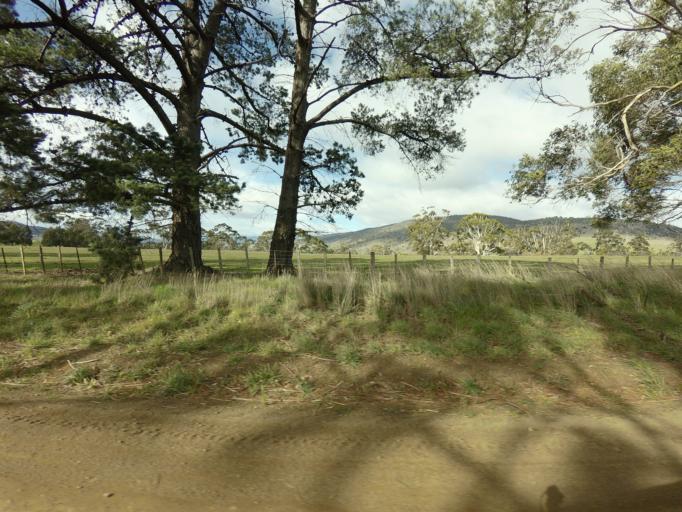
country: AU
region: Tasmania
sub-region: Derwent Valley
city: New Norfolk
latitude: -42.7142
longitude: 146.8865
